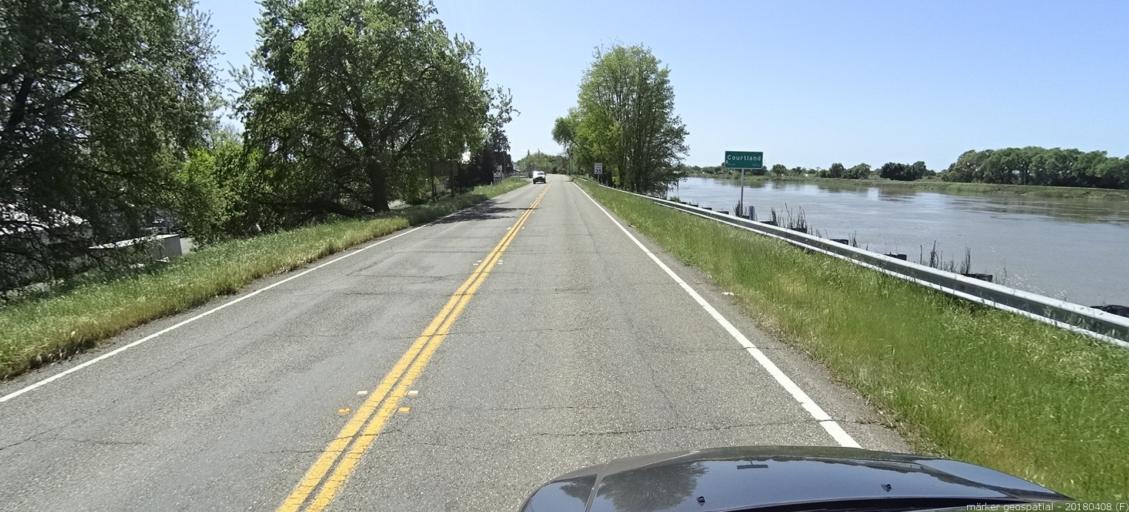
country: US
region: California
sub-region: Sacramento County
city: Walnut Grove
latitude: 38.3338
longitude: -121.5678
